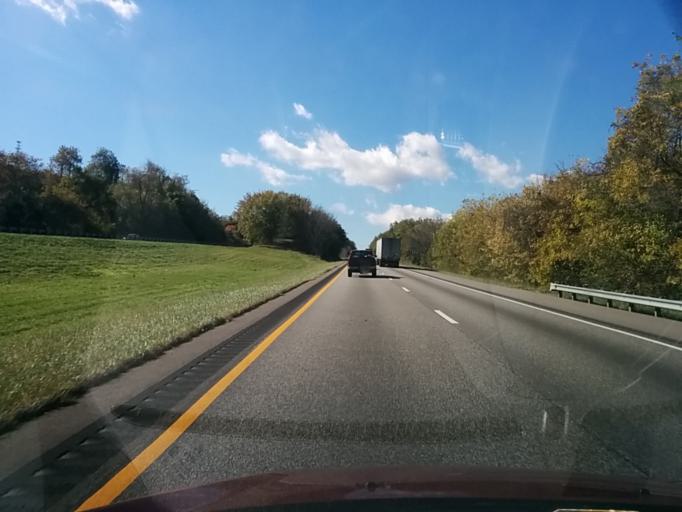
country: US
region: Virginia
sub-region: Botetourt County
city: Buchanan
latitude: 37.4874
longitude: -79.7725
